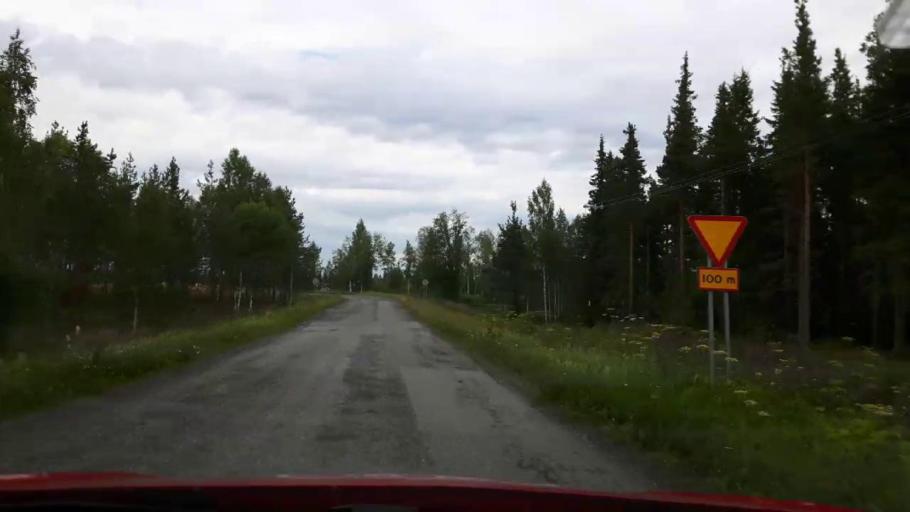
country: SE
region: Jaemtland
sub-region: Stroemsunds Kommun
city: Stroemsund
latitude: 63.5361
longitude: 15.3544
